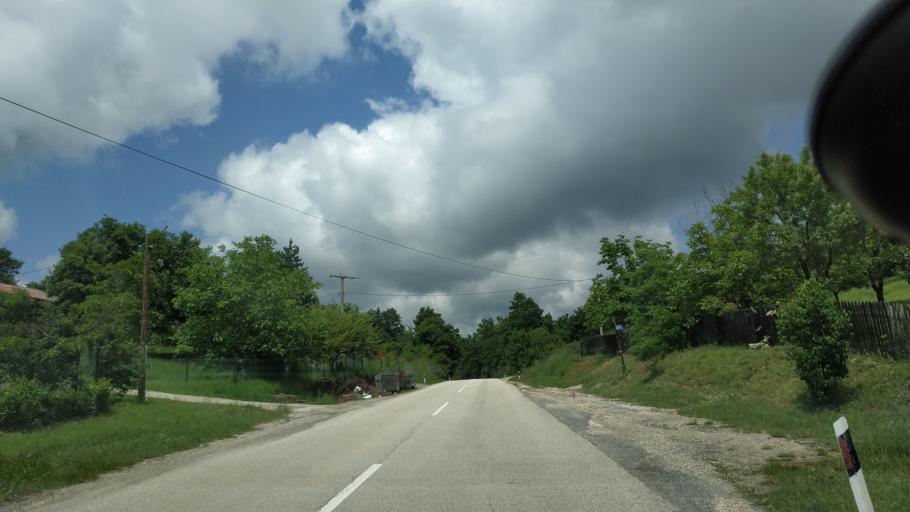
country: RS
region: Central Serbia
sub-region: Borski Okrug
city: Bor
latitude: 44.0849
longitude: 22.0075
